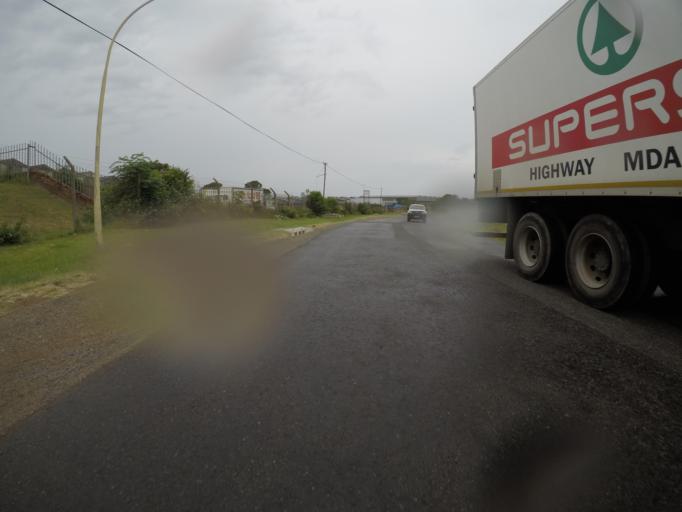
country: ZA
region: Eastern Cape
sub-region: Buffalo City Metropolitan Municipality
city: East London
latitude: -32.9742
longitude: 27.8236
